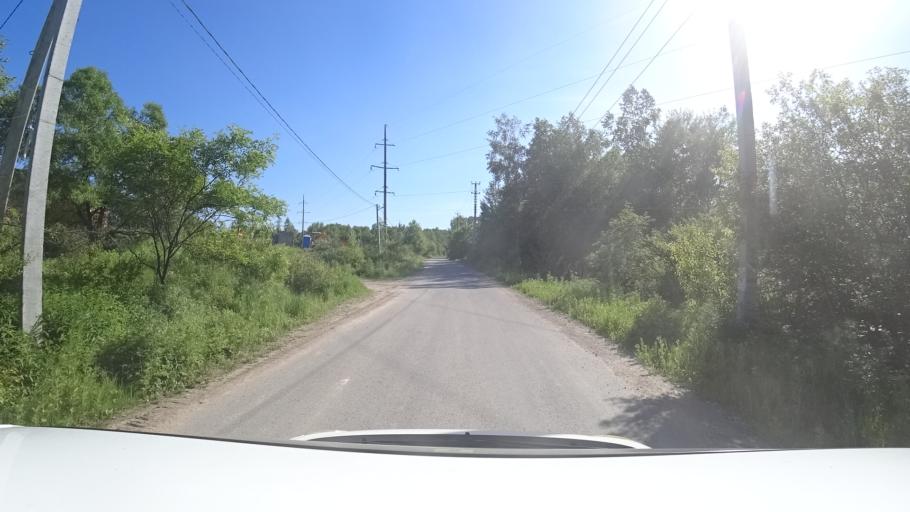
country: RU
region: Khabarovsk Krai
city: Topolevo
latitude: 48.5471
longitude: 135.1854
